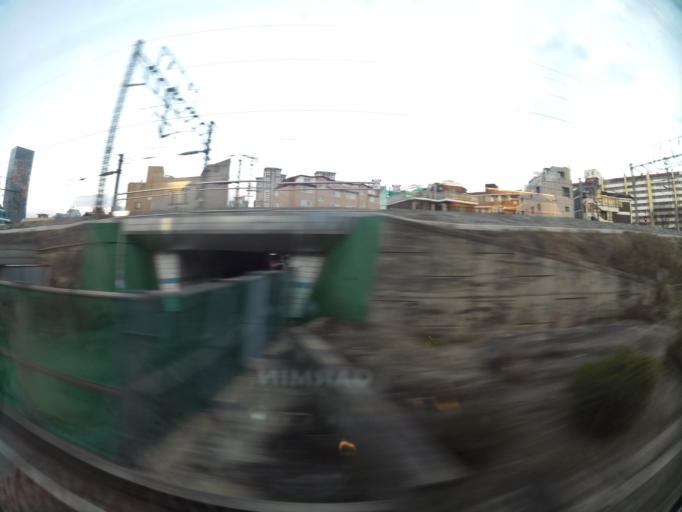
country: KR
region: Gyeonggi-do
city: Kwangmyong
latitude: 37.5145
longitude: 126.9219
